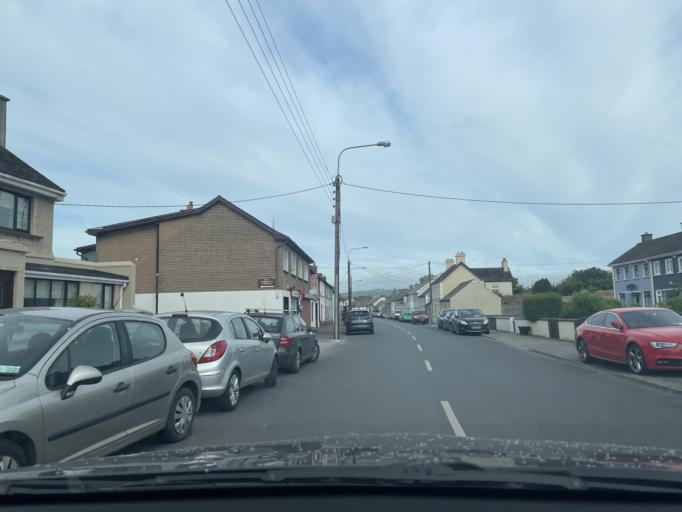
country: IE
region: Leinster
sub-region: County Carlow
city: Bagenalstown
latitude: 52.7017
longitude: -6.9525
